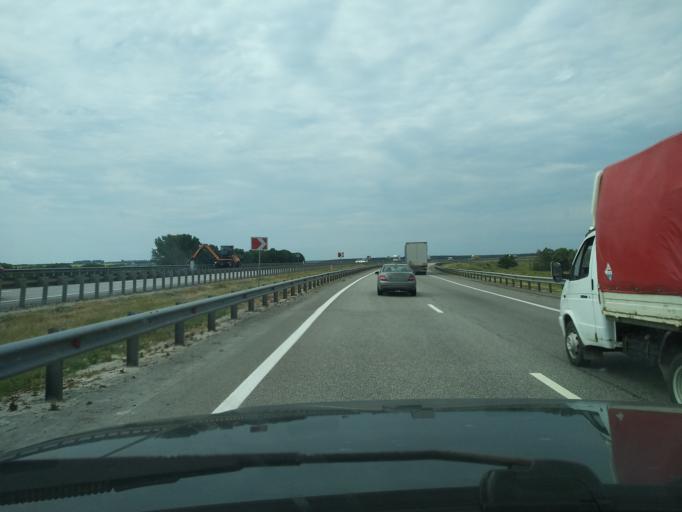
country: RU
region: Lipetsk
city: Khlevnoye
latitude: 52.0620
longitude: 39.1814
